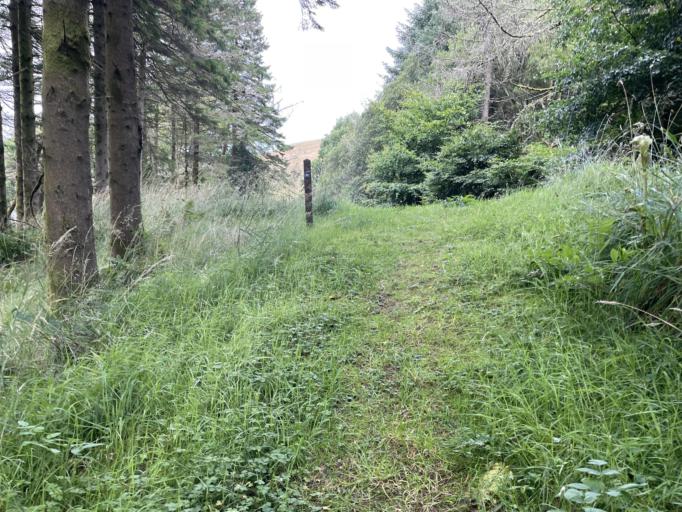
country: GB
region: Scotland
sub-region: South Ayrshire
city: Maybole
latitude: 55.2070
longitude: -4.6732
